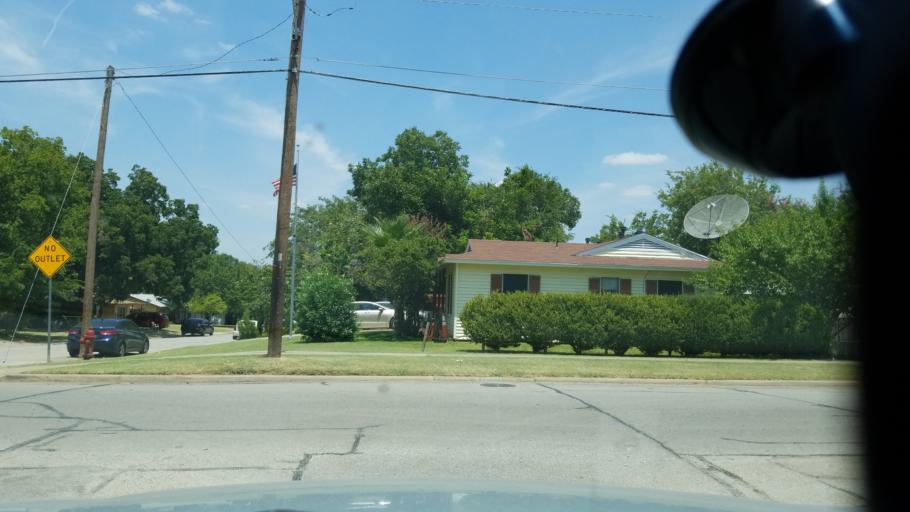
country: US
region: Texas
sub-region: Dallas County
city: Grand Prairie
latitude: 32.7556
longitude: -96.9725
